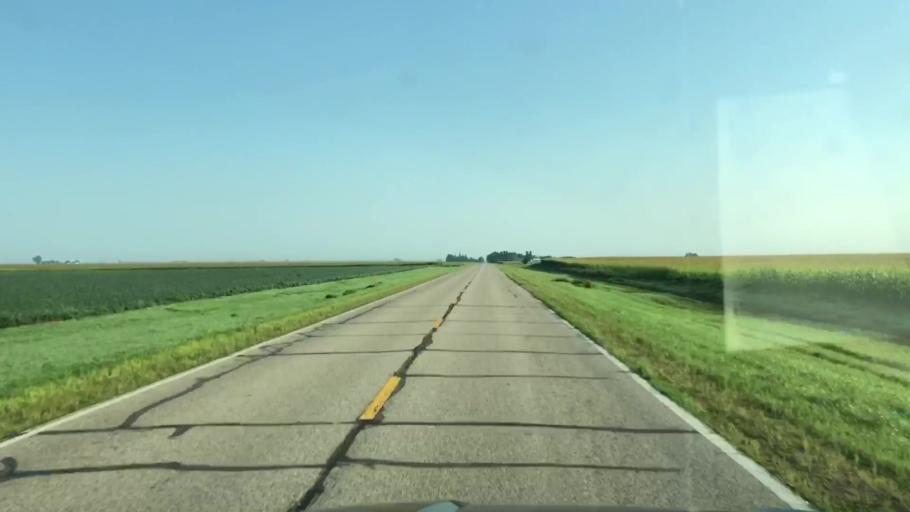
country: US
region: Iowa
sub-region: Lyon County
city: George
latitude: 43.4153
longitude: -95.9982
